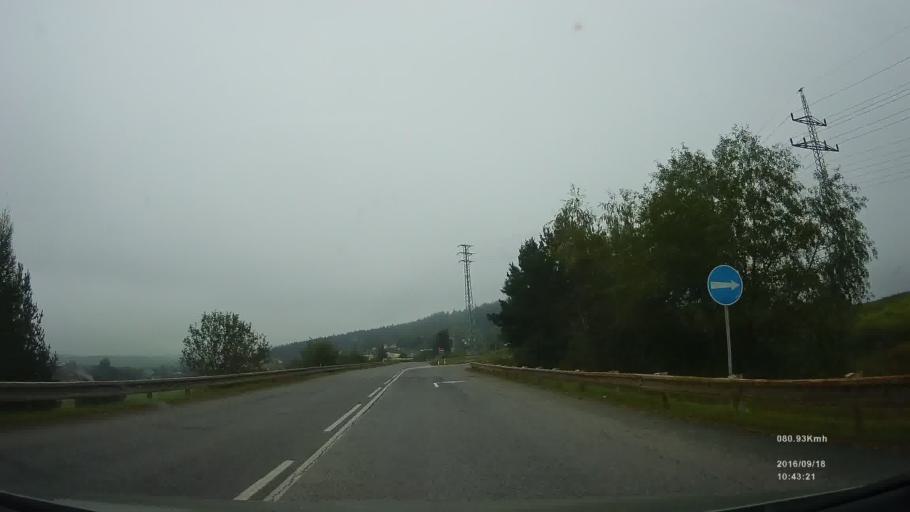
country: SK
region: Kosicky
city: Spisska Nova Ves
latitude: 48.9482
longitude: 20.5801
